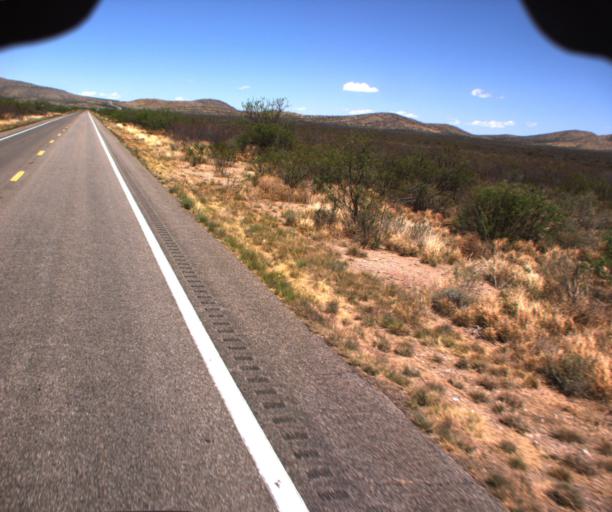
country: US
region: Arizona
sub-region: Cochise County
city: Tombstone
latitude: 31.6293
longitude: -110.0472
